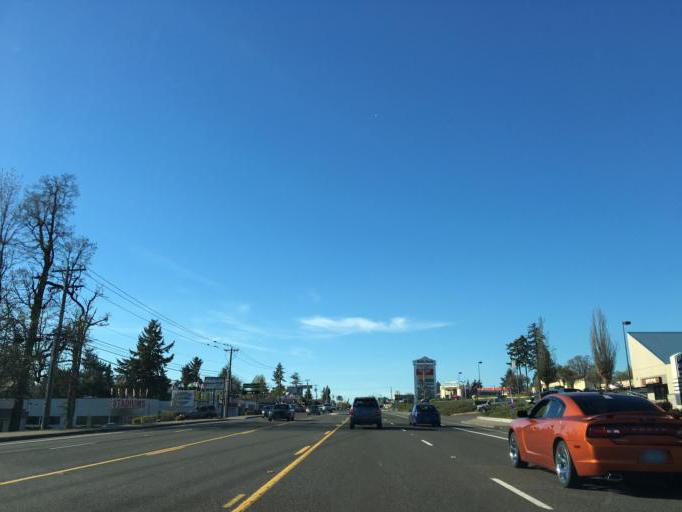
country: US
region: Oregon
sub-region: Clackamas County
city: Jennings Lodge
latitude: 45.4057
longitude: -122.6240
